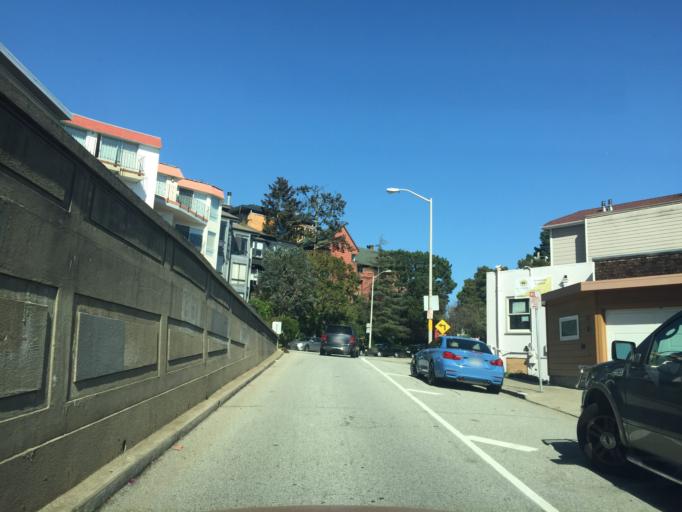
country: US
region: California
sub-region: San Francisco County
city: San Francisco
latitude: 37.7631
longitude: -122.4440
